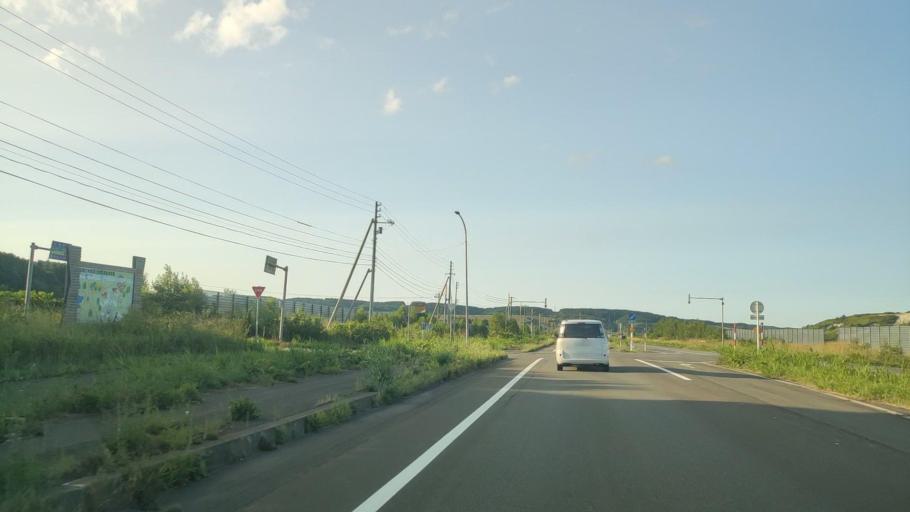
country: JP
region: Hokkaido
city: Wakkanai
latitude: 45.3258
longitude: 141.7197
